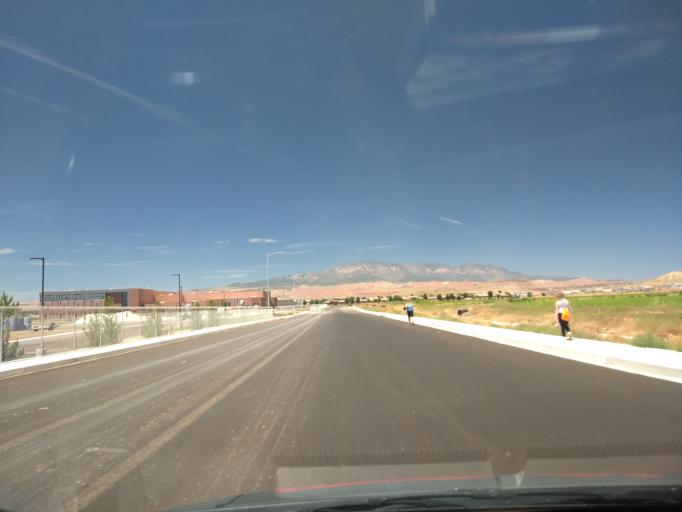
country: US
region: Utah
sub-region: Washington County
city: Washington
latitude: 37.0702
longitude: -113.5063
